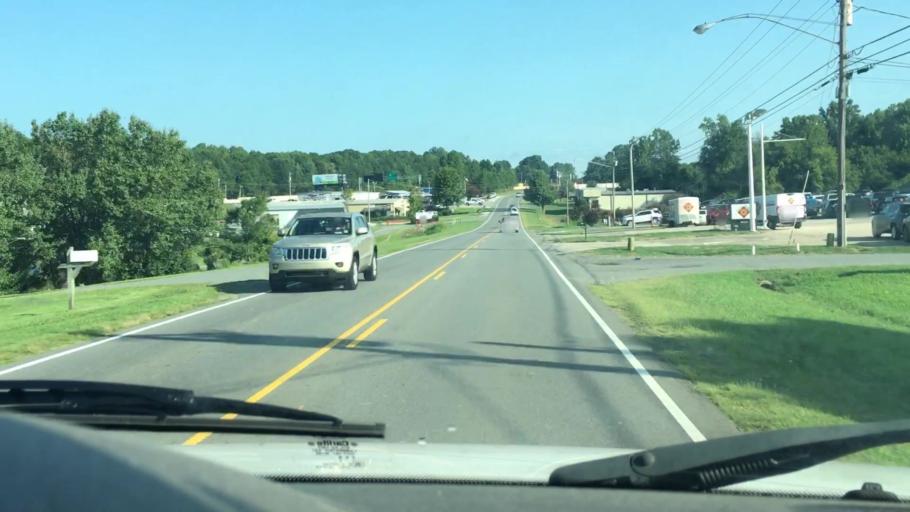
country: US
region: North Carolina
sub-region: Mecklenburg County
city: Cornelius
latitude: 35.4690
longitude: -80.8728
